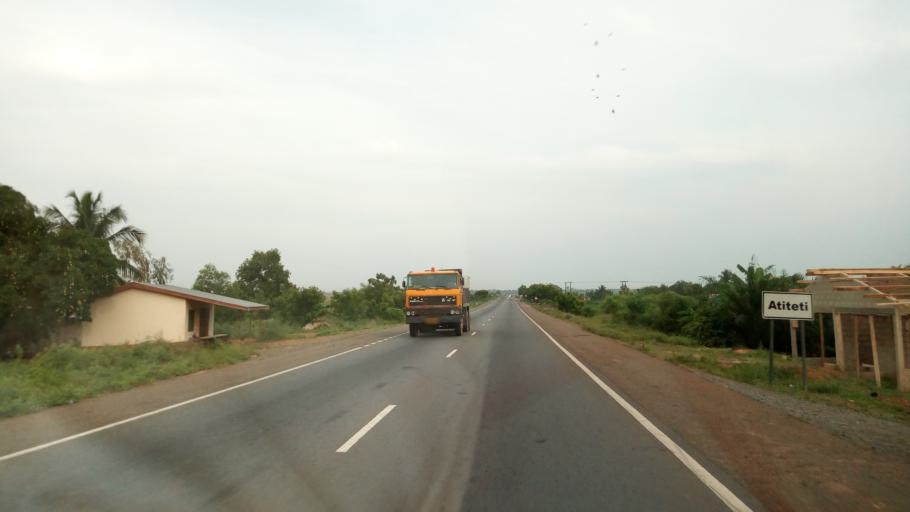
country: GH
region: Volta
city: Keta
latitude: 6.0532
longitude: 0.9668
